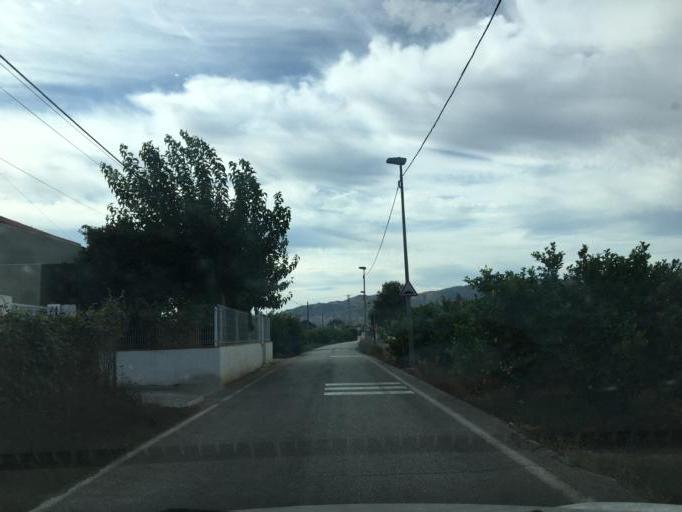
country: ES
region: Murcia
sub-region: Murcia
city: Santomera
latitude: 38.0162
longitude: -1.0467
